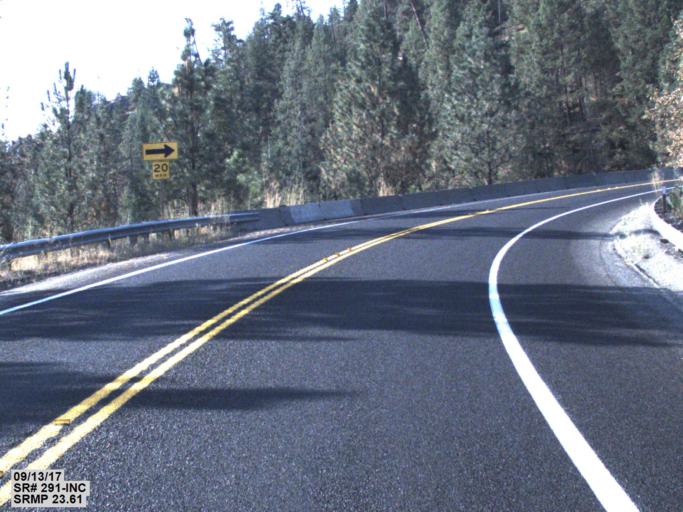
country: US
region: Washington
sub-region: Spokane County
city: Deer Park
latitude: 47.8770
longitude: -117.7020
